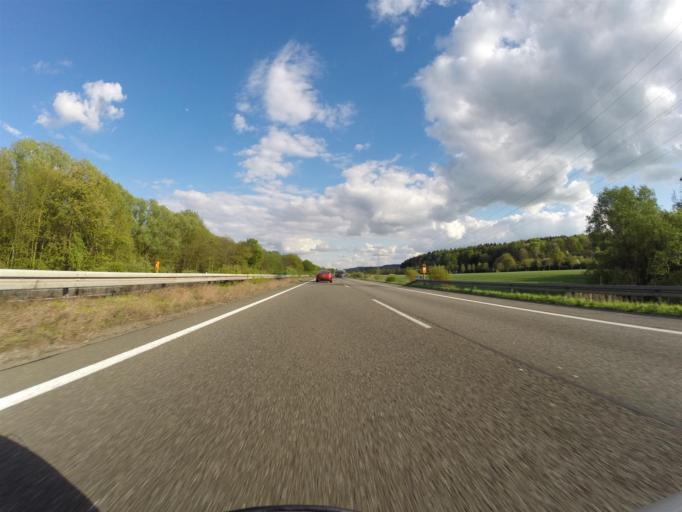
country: DE
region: Saarland
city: Beckingen
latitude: 49.3990
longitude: 6.6607
